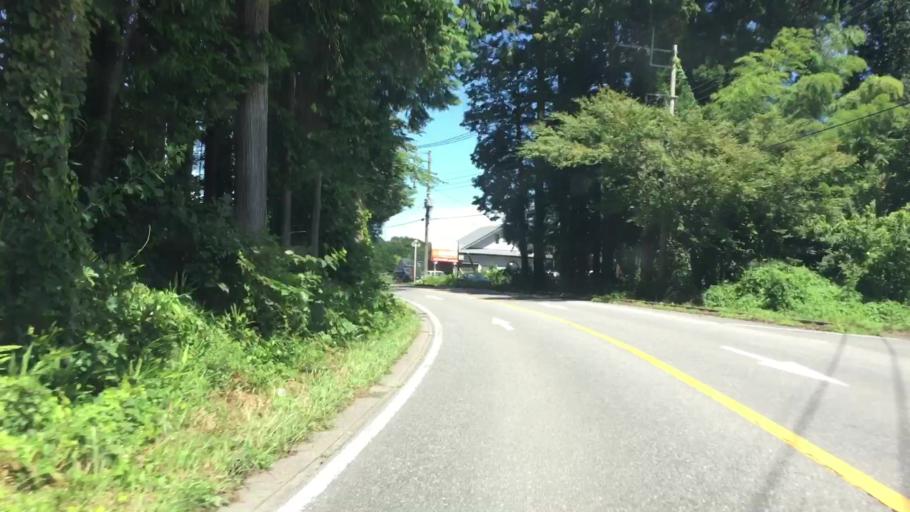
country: JP
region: Tochigi
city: Imaichi
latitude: 36.7142
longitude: 139.7522
